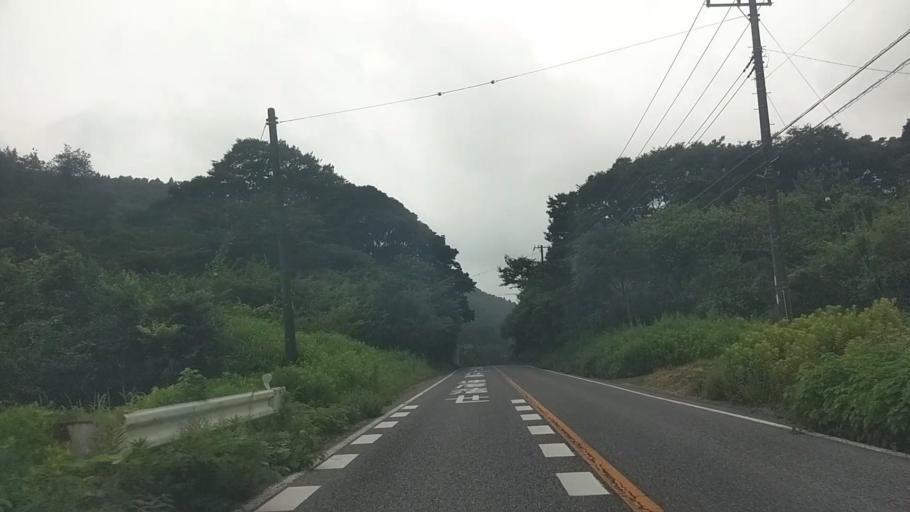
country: JP
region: Chiba
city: Tateyama
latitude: 35.1418
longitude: 139.9133
